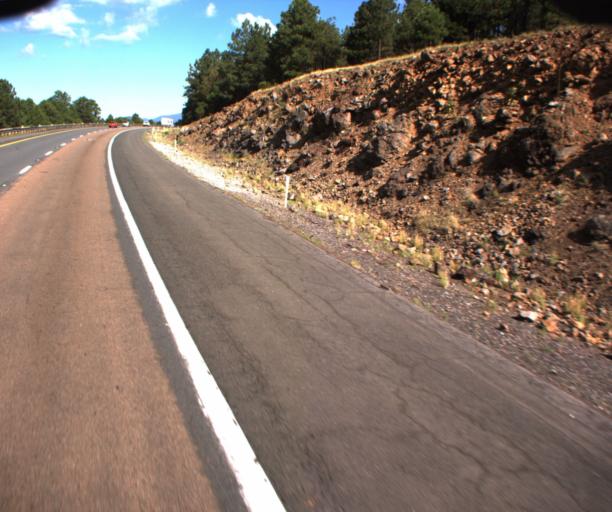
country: US
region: Arizona
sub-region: Coconino County
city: Flagstaff
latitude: 35.2035
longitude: -111.7654
